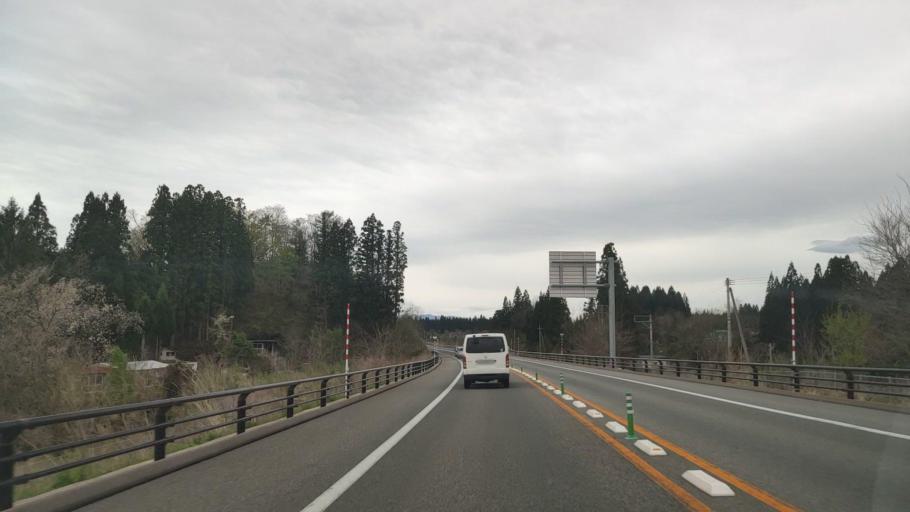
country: JP
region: Akita
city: Odate
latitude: 40.3155
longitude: 140.5819
